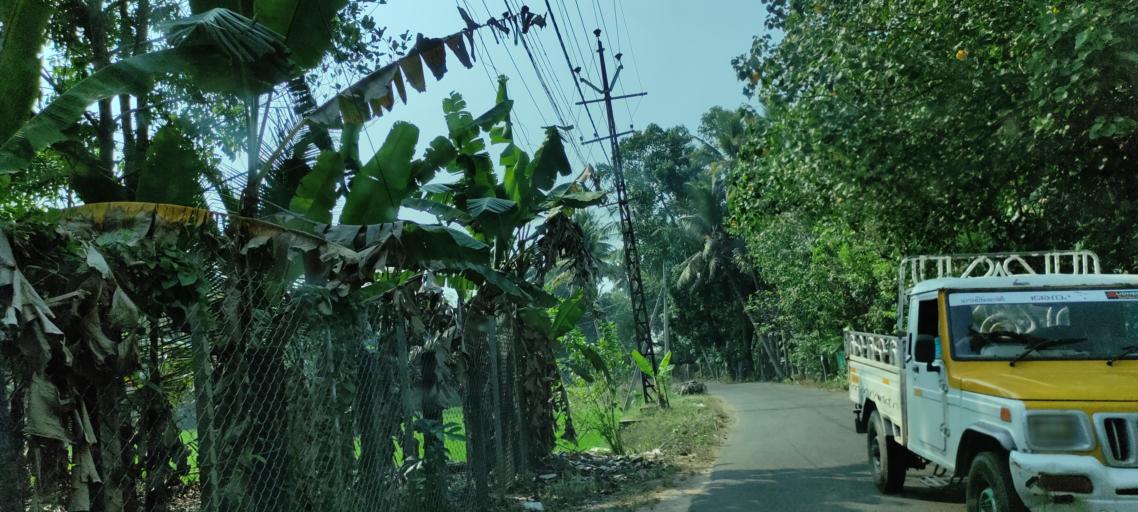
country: IN
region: Kerala
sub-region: Pattanamtitta
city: Tiruvalla
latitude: 9.3605
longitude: 76.5058
